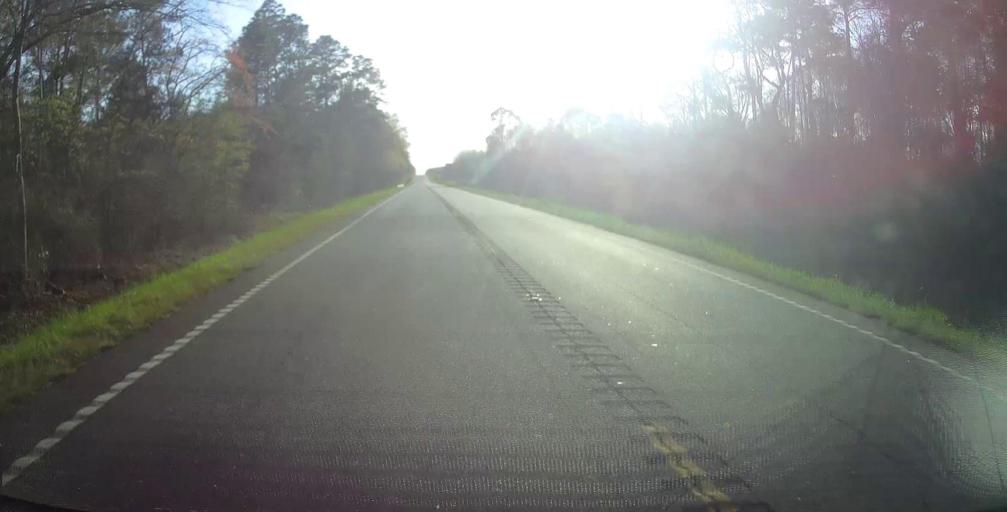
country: US
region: Georgia
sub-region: Tattnall County
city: Reidsville
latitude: 32.1193
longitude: -82.0698
